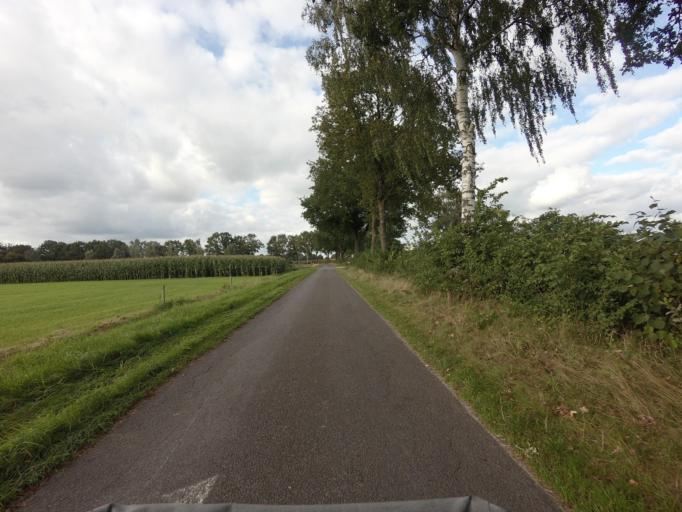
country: NL
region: Overijssel
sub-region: Gemeente Deventer
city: Schalkhaar
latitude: 52.2744
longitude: 6.2561
